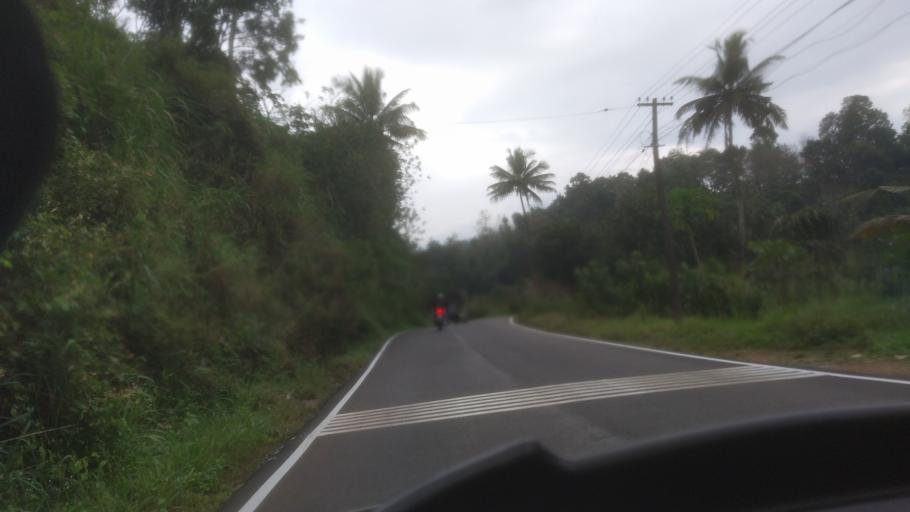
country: IN
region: Kerala
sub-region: Idukki
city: Idukki
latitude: 9.9427
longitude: 77.0218
